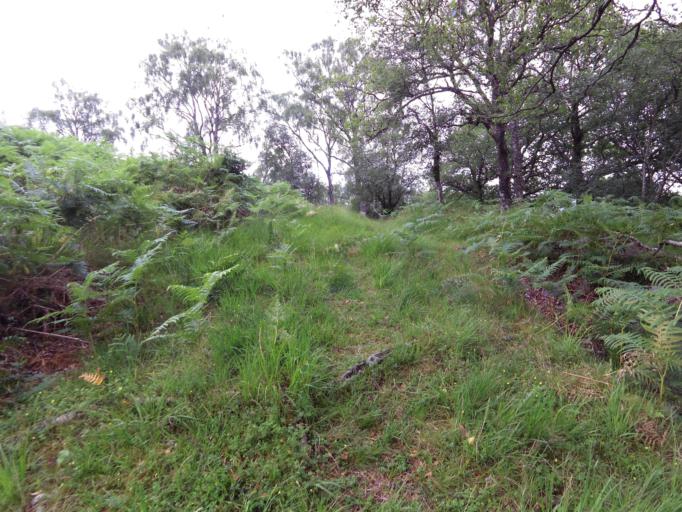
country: GB
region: Scotland
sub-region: Highland
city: Fort William
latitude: 56.8306
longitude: -5.1272
